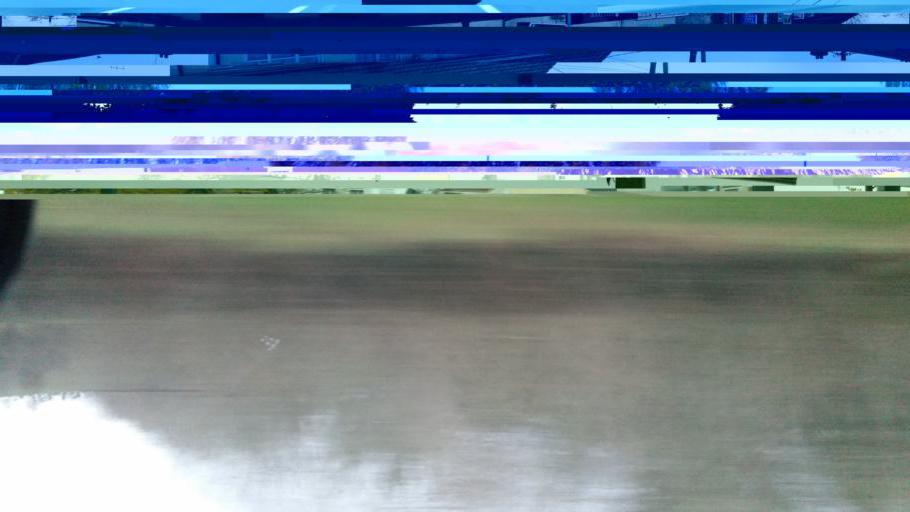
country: IE
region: Ulster
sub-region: County Monaghan
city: Monaghan
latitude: 54.4356
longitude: -6.9952
